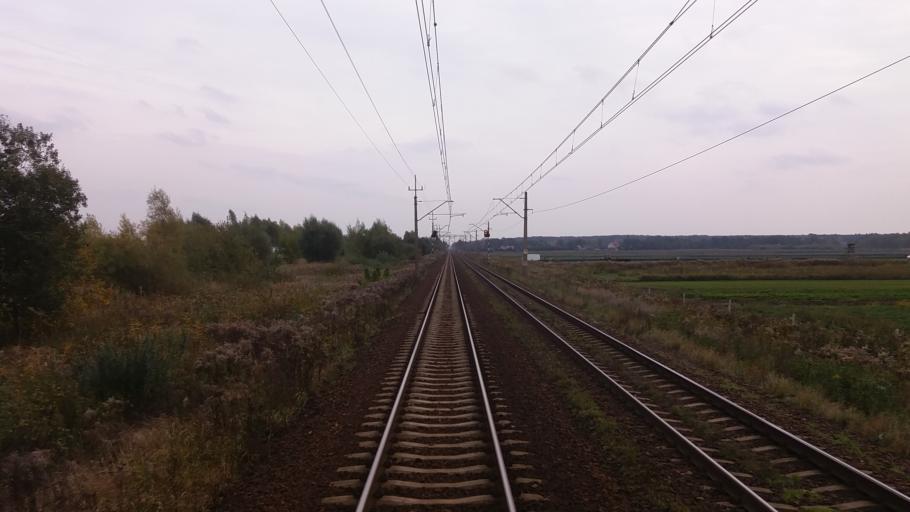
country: PL
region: West Pomeranian Voivodeship
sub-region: Powiat gryfinski
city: Stare Czarnowo
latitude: 53.3872
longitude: 14.7262
